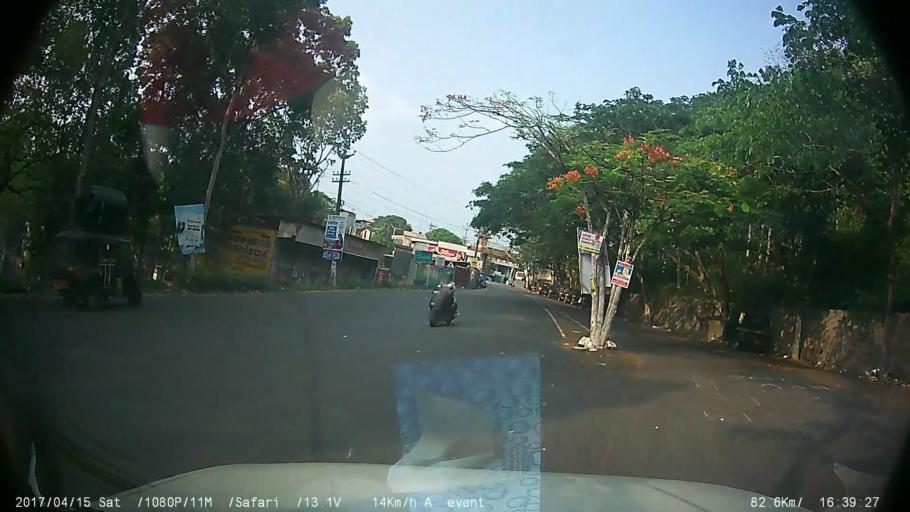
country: IN
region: Kerala
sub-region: Kottayam
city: Kottayam
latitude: 9.6474
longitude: 76.5199
